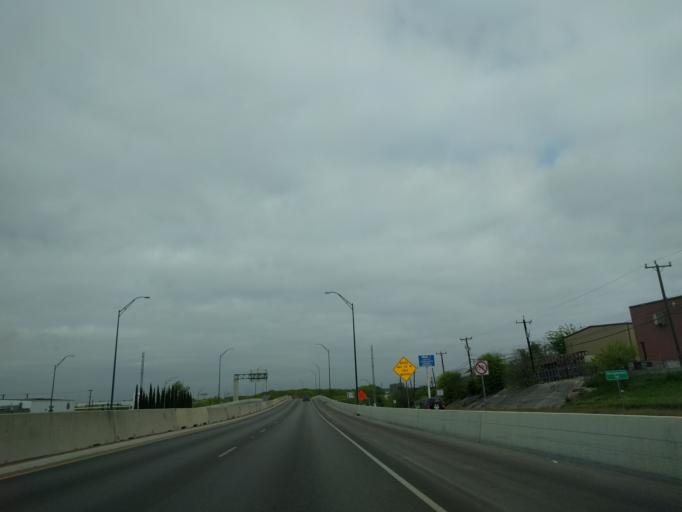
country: US
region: Texas
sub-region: Bexar County
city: Windcrest
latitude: 29.5394
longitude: -98.4194
